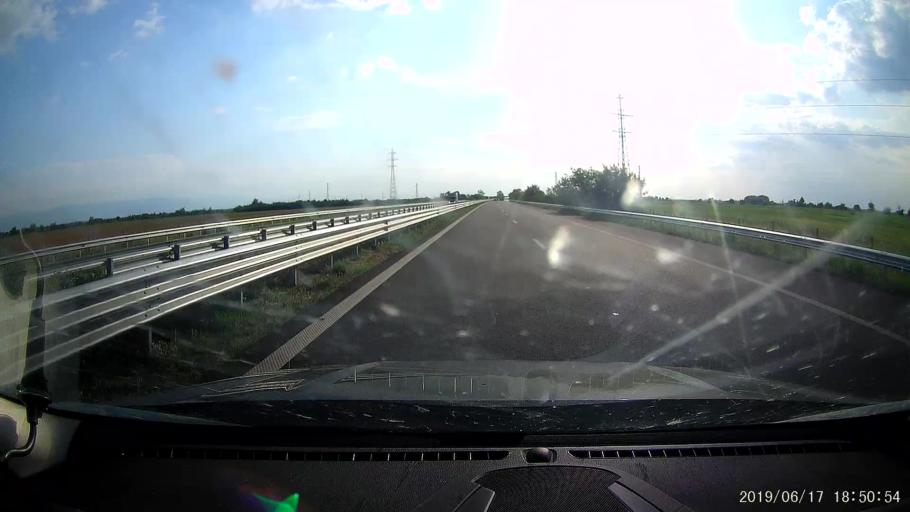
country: BG
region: Plovdiv
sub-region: Obshtina Rakovski
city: Rakovski
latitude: 42.2137
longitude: 24.9874
